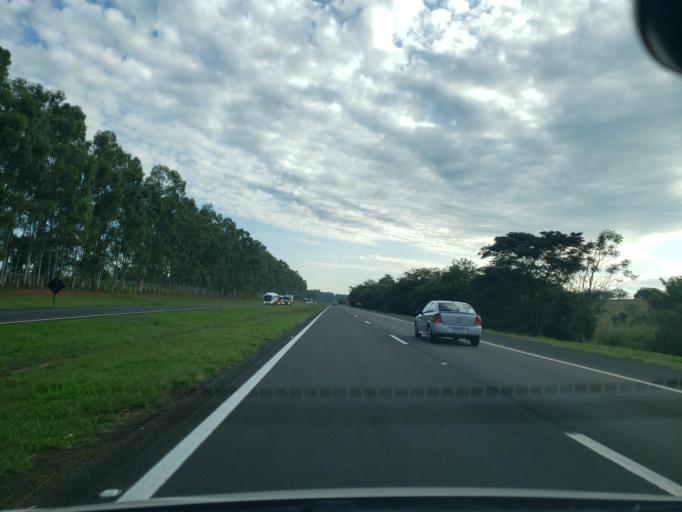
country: BR
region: Sao Paulo
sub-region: Guararapes
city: Guararapes
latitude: -21.2116
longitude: -50.6752
